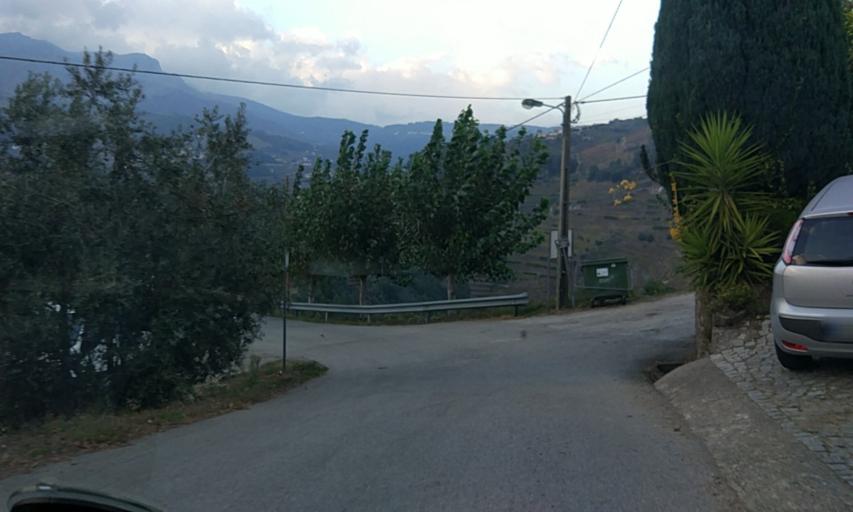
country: PT
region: Vila Real
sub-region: Mesao Frio
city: Mesao Frio
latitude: 41.1811
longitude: -7.8448
